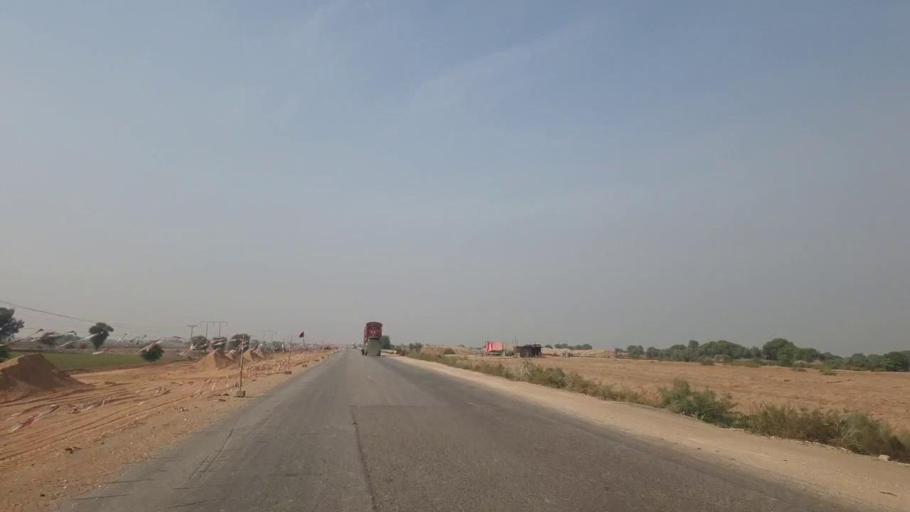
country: PK
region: Sindh
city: Sann
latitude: 26.1397
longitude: 68.0398
